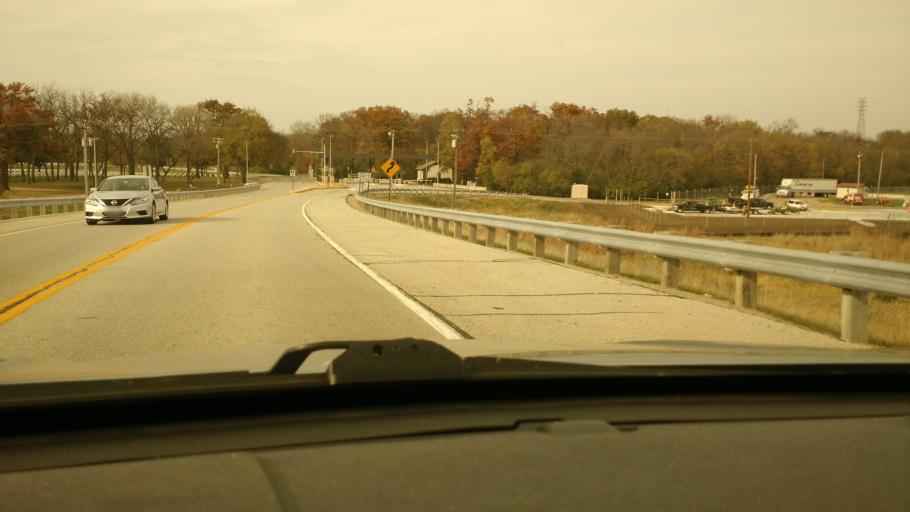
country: US
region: Illinois
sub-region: Rock Island County
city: Moline
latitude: 41.5118
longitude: -90.5198
